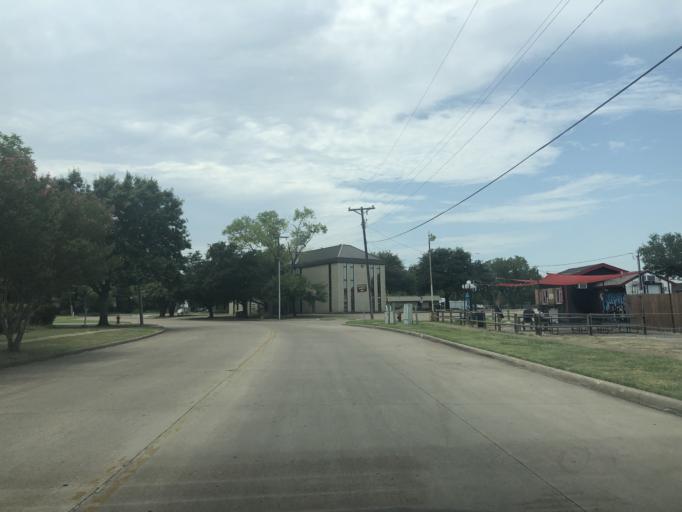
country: US
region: Texas
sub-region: Dallas County
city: Grand Prairie
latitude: 32.7432
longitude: -97.0043
